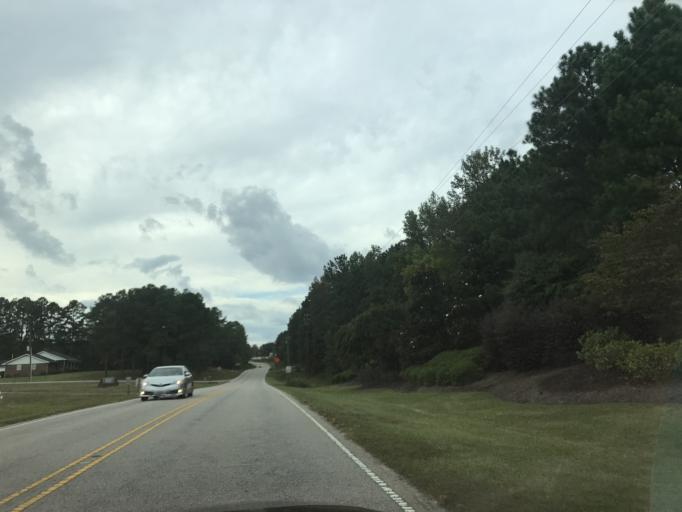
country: US
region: North Carolina
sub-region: Wake County
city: Rolesville
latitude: 35.9792
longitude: -78.3777
